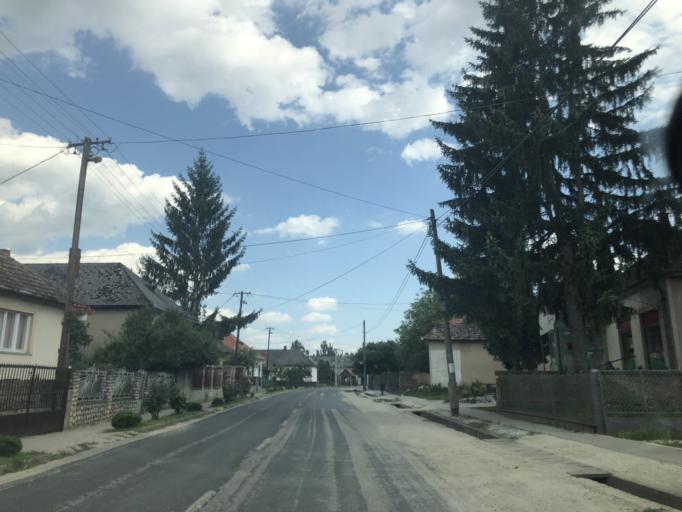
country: HU
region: Borsod-Abauj-Zemplen
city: Szendro
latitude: 48.4399
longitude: 20.7945
